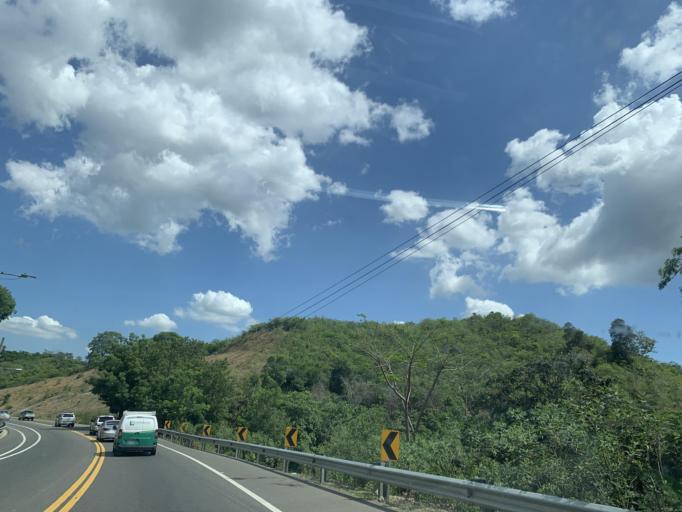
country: DO
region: Puerto Plata
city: Altamira
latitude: 19.6214
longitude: -70.8468
